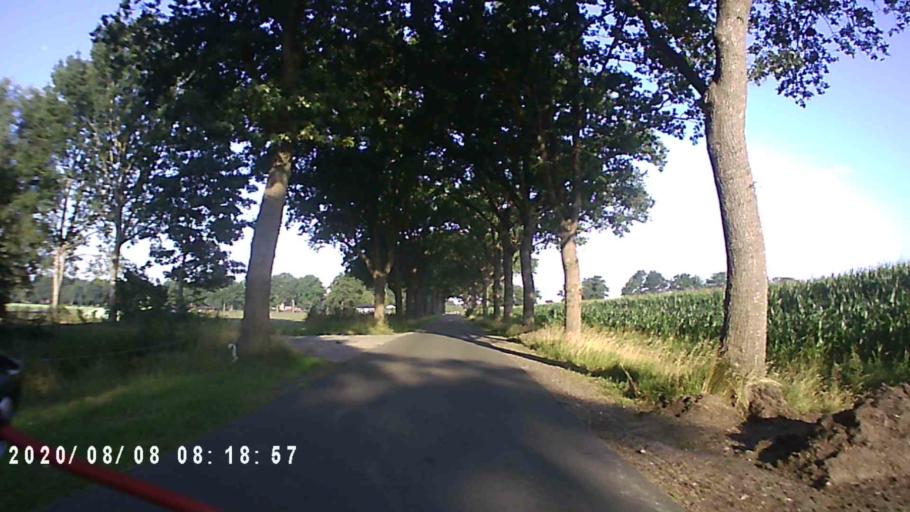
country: NL
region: Groningen
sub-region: Gemeente Leek
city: Leek
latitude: 53.0965
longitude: 6.3196
